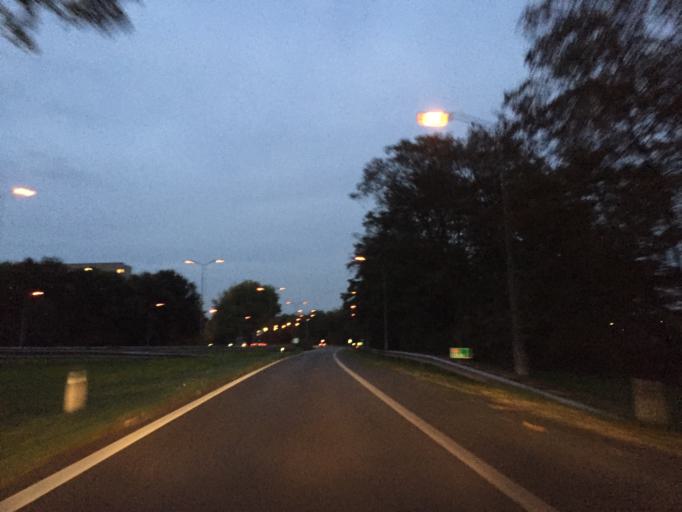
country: NL
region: Gelderland
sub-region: Gemeente Maasdriel
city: Hedel
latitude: 51.6954
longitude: 5.2475
